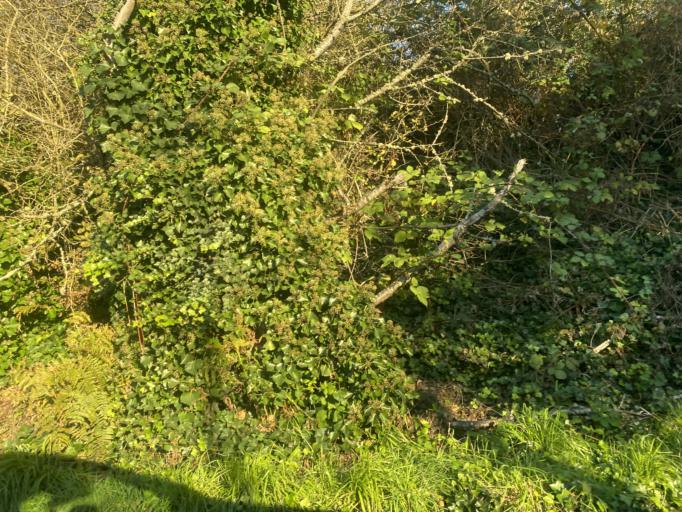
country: US
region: Washington
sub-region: King County
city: Seattle
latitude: 47.6489
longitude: -122.3958
